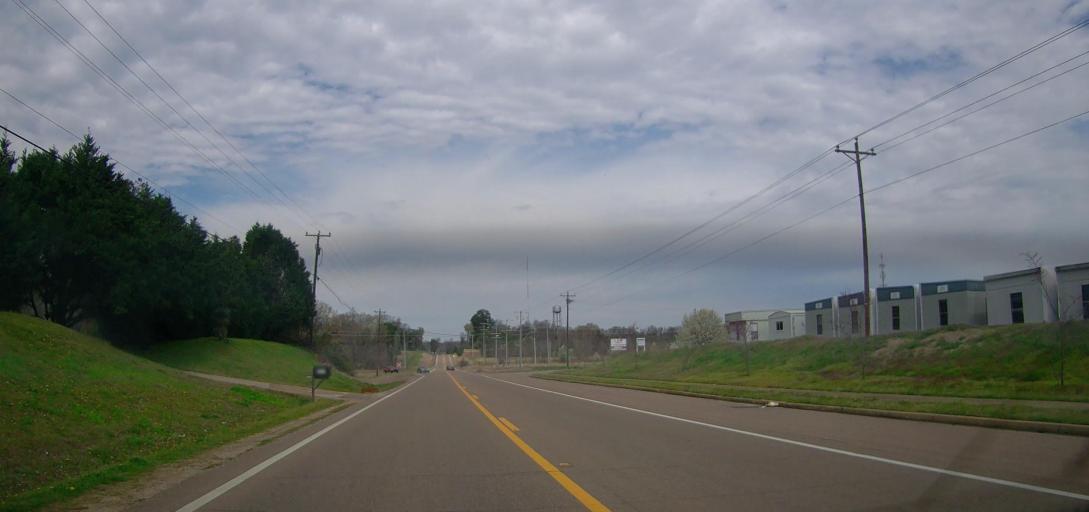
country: US
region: Mississippi
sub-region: De Soto County
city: Olive Branch
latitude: 34.9819
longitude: -89.8572
